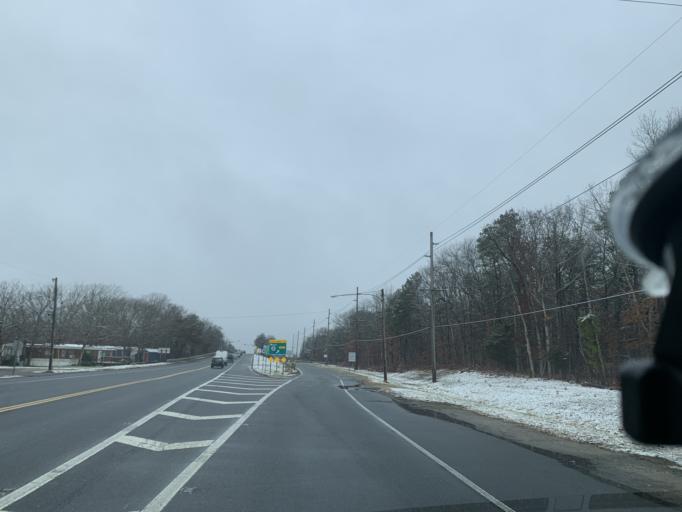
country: US
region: New Jersey
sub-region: Atlantic County
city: Pomona
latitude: 39.4326
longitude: -74.5821
